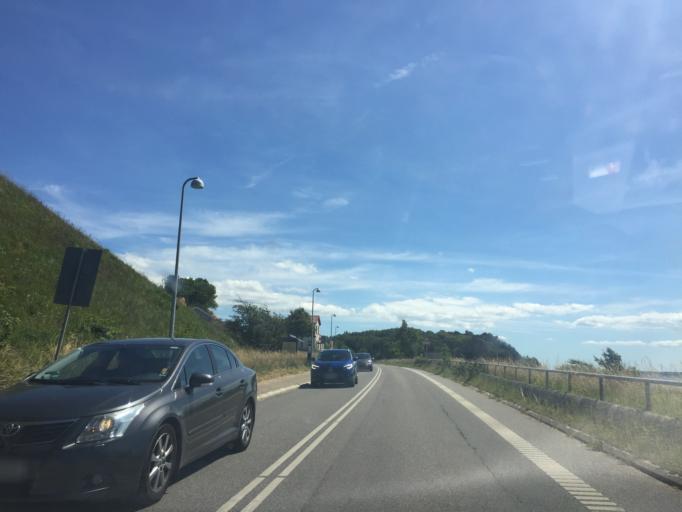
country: DK
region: Capital Region
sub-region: Halsnaes Kommune
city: Frederiksvaerk
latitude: 55.9576
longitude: 12.0204
